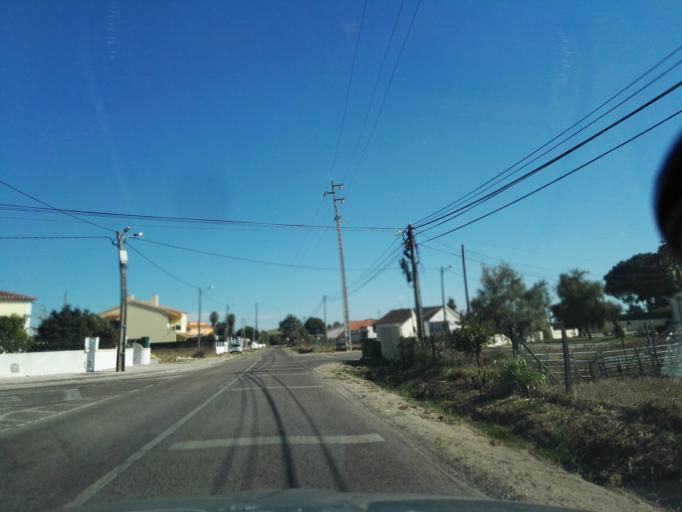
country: PT
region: Santarem
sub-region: Benavente
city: Benavente
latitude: 38.9421
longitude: -8.8024
